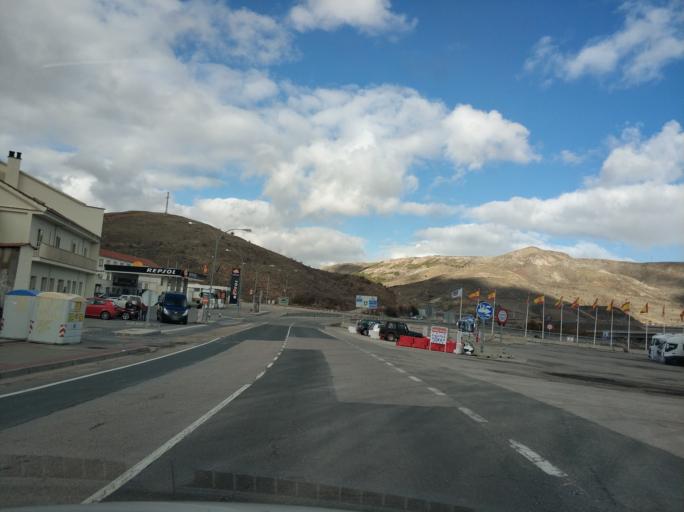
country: ES
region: Castille and Leon
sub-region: Provincia de Soria
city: Medinaceli
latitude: 41.1681
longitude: -2.4208
